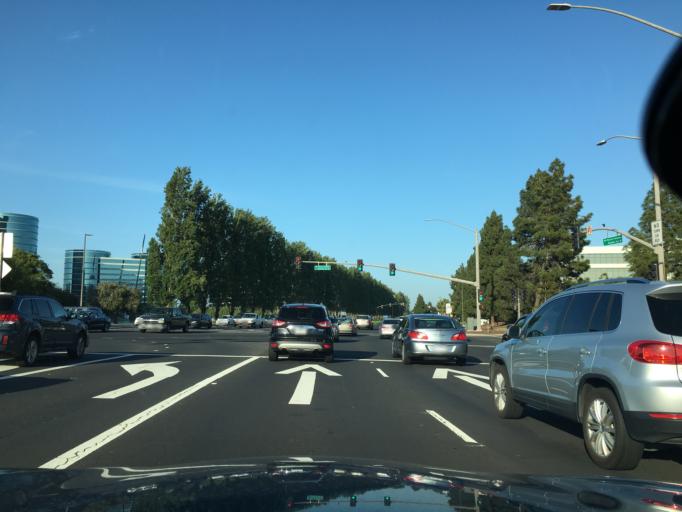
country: US
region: California
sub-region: San Mateo County
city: Belmont
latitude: 37.5283
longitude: -122.2669
